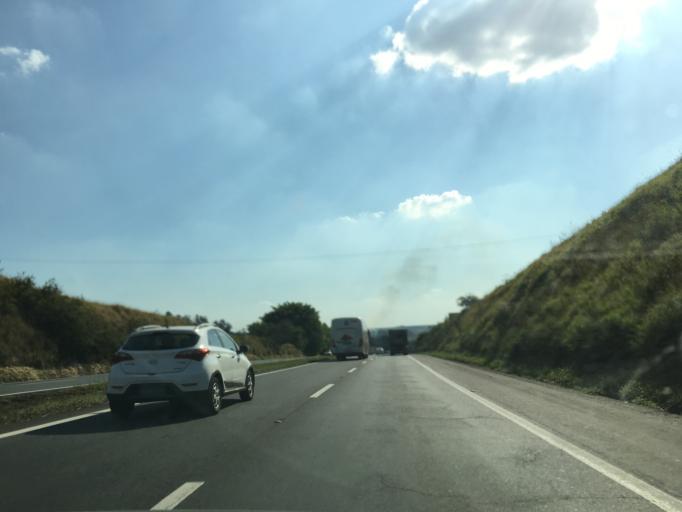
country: BR
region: Sao Paulo
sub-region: Santa Barbara D'Oeste
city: Santa Barbara d'Oeste
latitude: -22.7466
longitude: -47.5090
